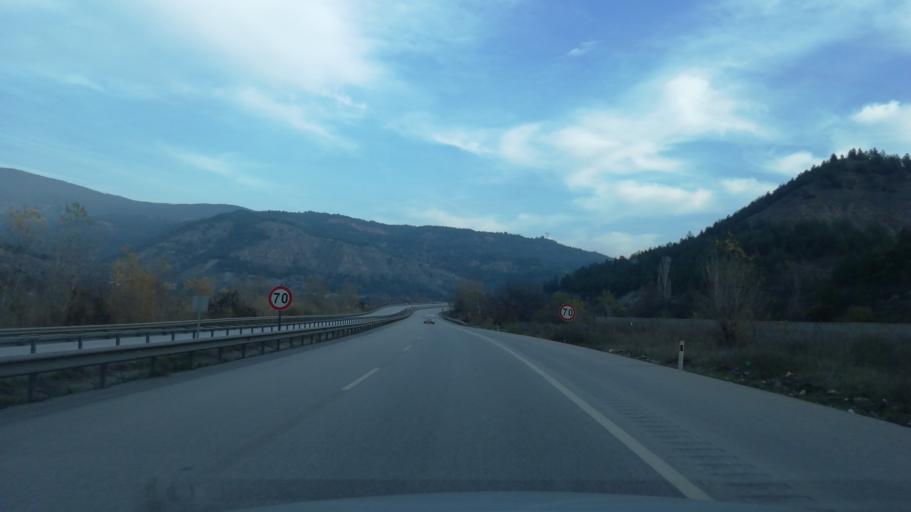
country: TR
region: Karabuk
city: Karabuk
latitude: 41.1507
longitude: 32.6596
